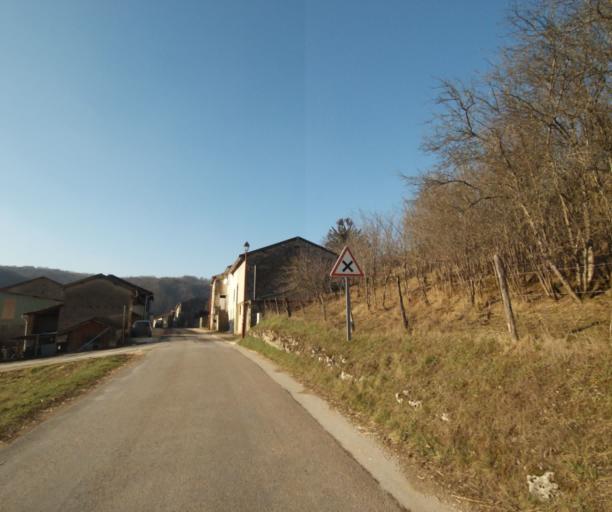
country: FR
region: Champagne-Ardenne
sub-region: Departement de la Haute-Marne
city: Joinville
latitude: 48.4920
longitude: 5.1961
